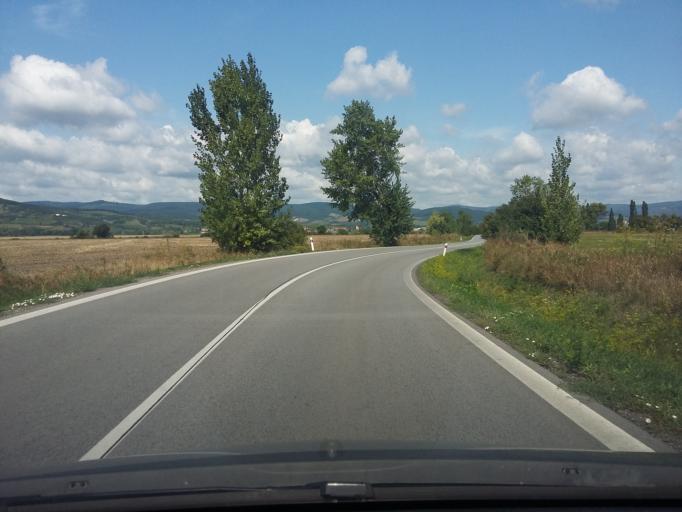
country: SK
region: Bratislavsky
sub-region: Okres Pezinok
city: Pezinok
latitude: 48.2518
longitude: 17.2618
